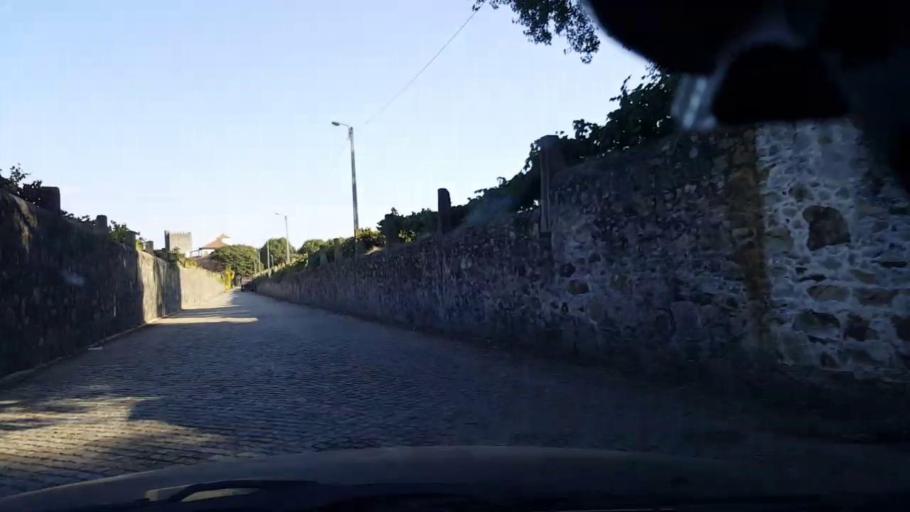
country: PT
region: Porto
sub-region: Vila do Conde
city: Arvore
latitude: 41.3401
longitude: -8.6844
